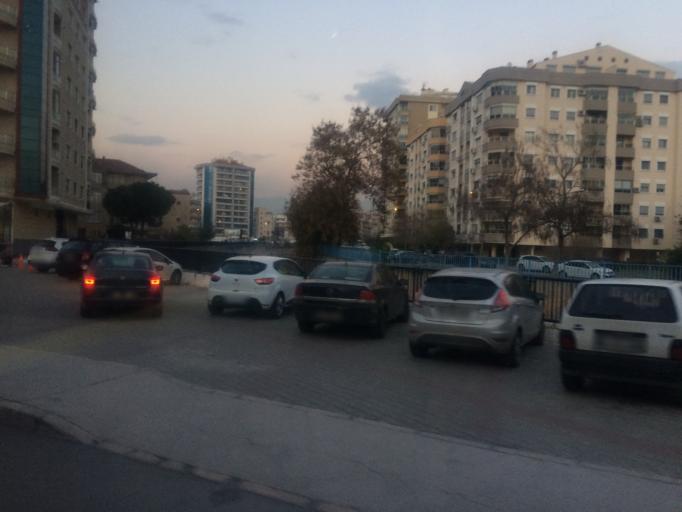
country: TR
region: Izmir
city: Karsiyaka
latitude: 38.4633
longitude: 27.0960
